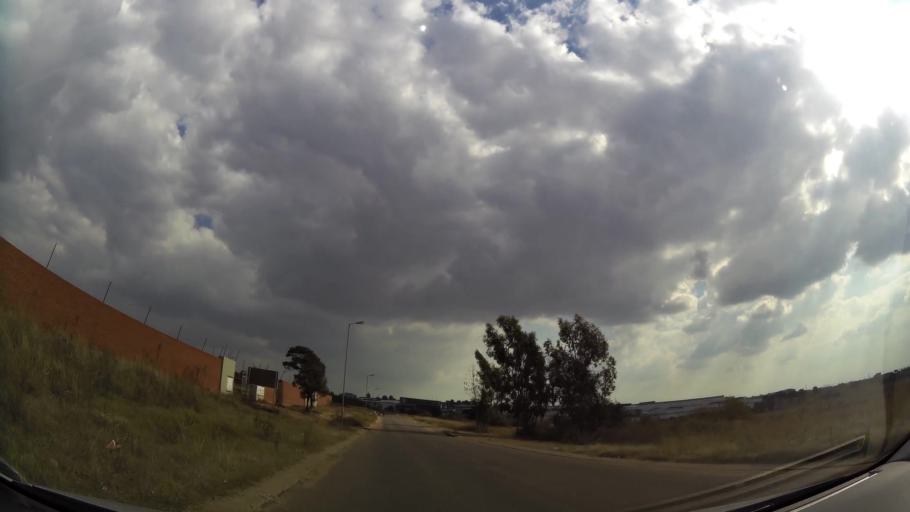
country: ZA
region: Gauteng
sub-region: City of Tshwane Metropolitan Municipality
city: Centurion
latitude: -25.9048
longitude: 28.1705
